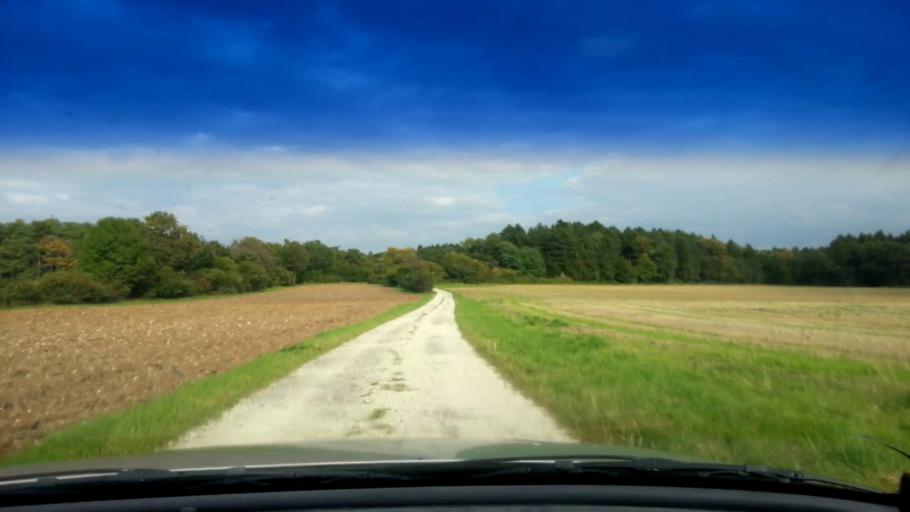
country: DE
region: Bavaria
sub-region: Upper Franconia
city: Wattendorf
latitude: 49.9898
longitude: 11.0892
